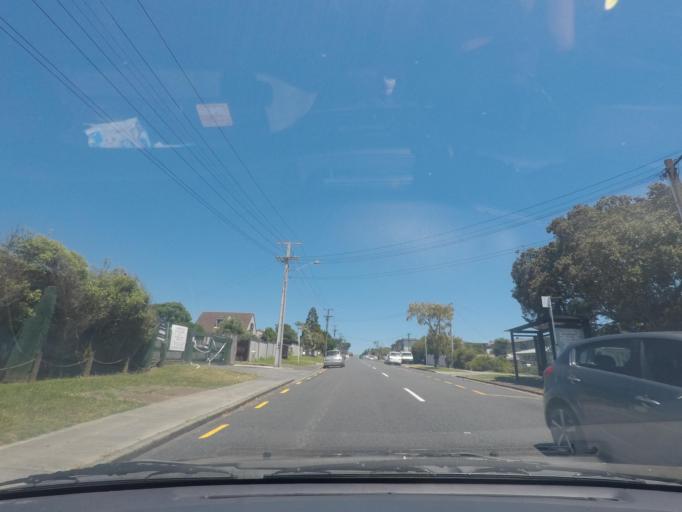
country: NZ
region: Auckland
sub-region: Auckland
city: Waitakere
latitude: -36.9182
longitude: 174.7146
